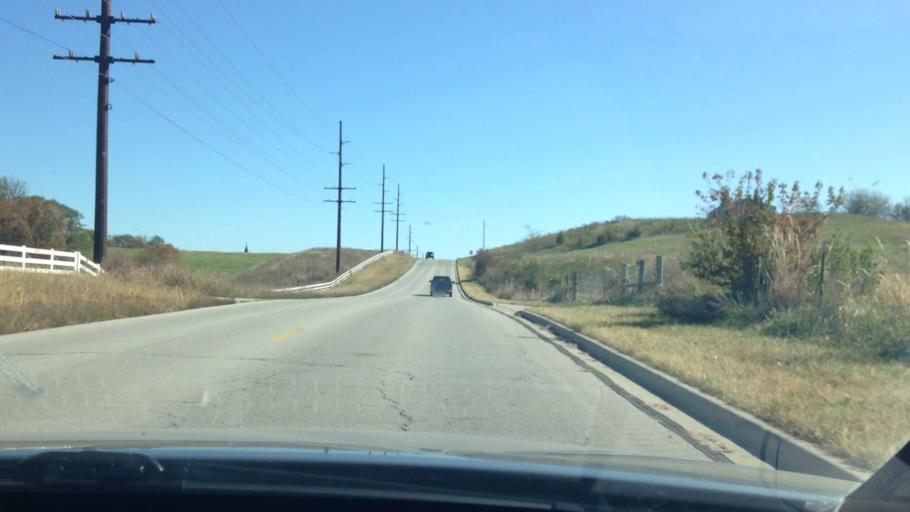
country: US
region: Missouri
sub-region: Platte County
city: Platte City
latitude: 39.3392
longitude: -94.7965
